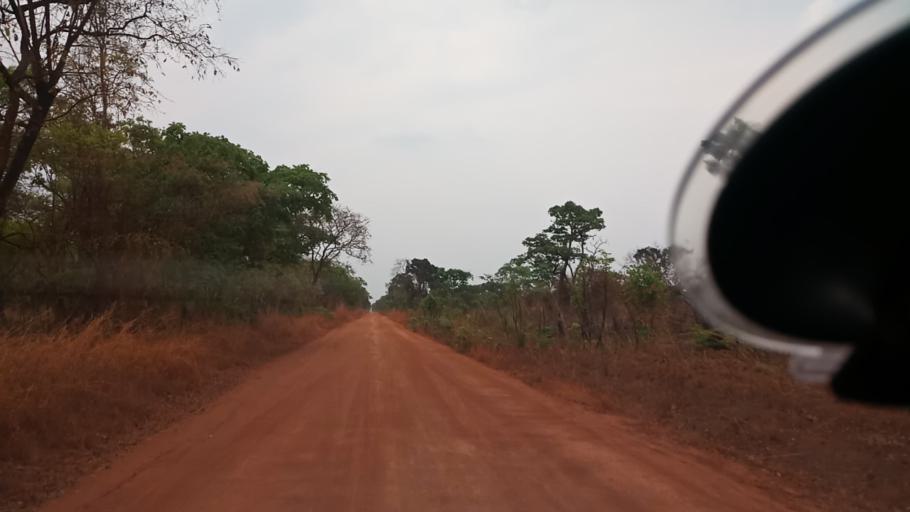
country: ZM
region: Luapula
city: Nchelenge
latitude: -9.4889
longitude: 28.2283
